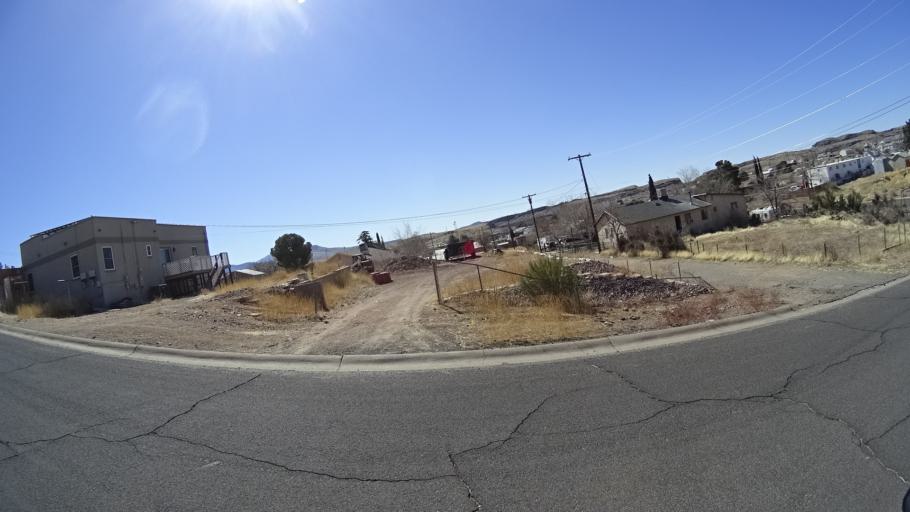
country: US
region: Arizona
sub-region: Mohave County
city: Kingman
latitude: 35.1966
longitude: -114.0592
